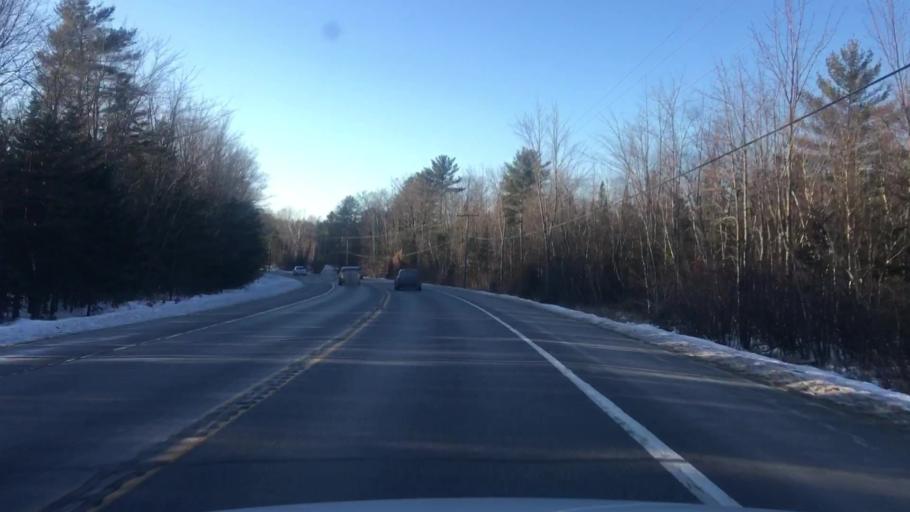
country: US
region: Maine
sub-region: Franklin County
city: New Sharon
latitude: 44.6454
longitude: -70.0246
